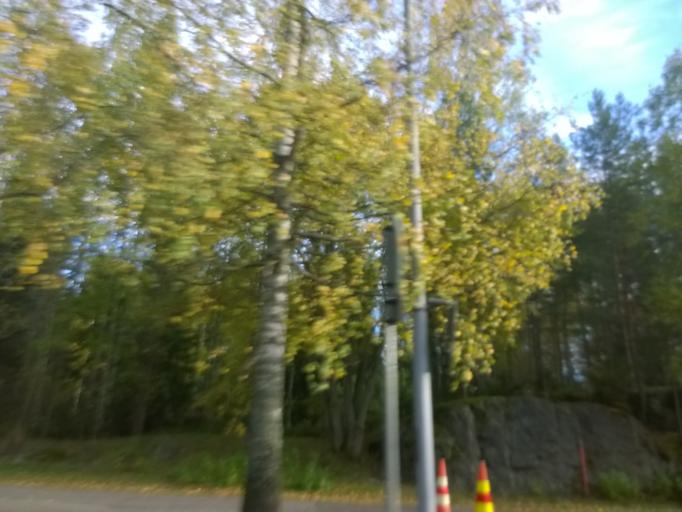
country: FI
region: Pirkanmaa
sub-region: Tampere
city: Tampere
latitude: 61.4502
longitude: 23.8335
